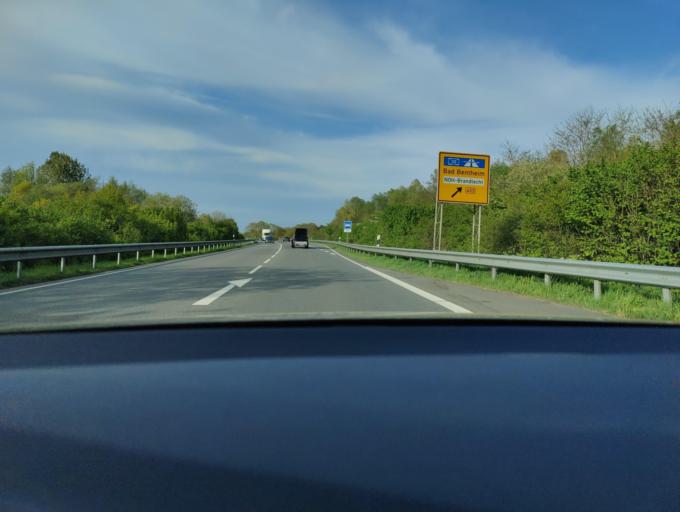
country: DE
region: Lower Saxony
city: Nordhorn
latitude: 52.4029
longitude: 7.0856
